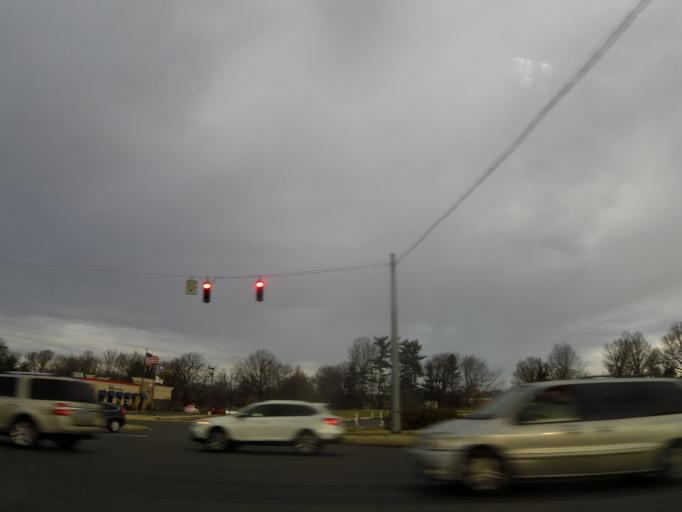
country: US
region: Kentucky
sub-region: McCracken County
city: Hendron
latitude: 37.0531
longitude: -88.6479
